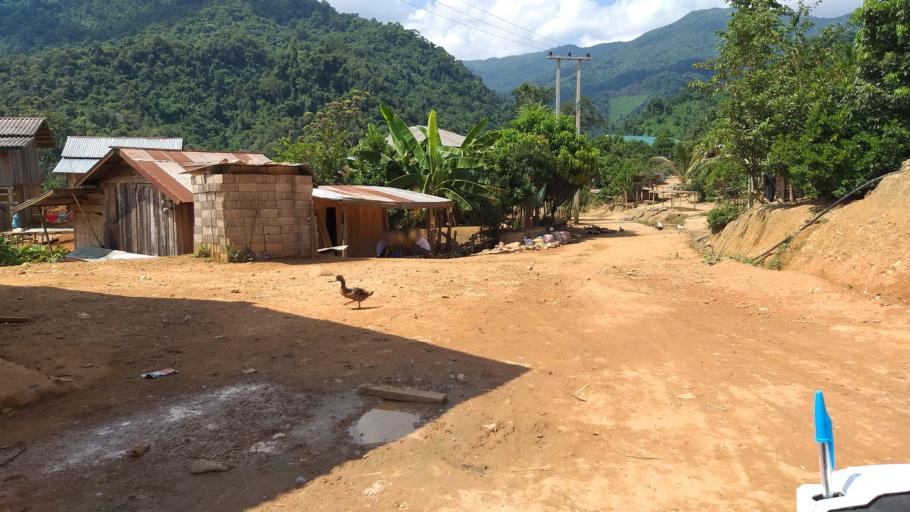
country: LA
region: Phongsali
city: Khoa
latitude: 21.3448
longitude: 102.5378
